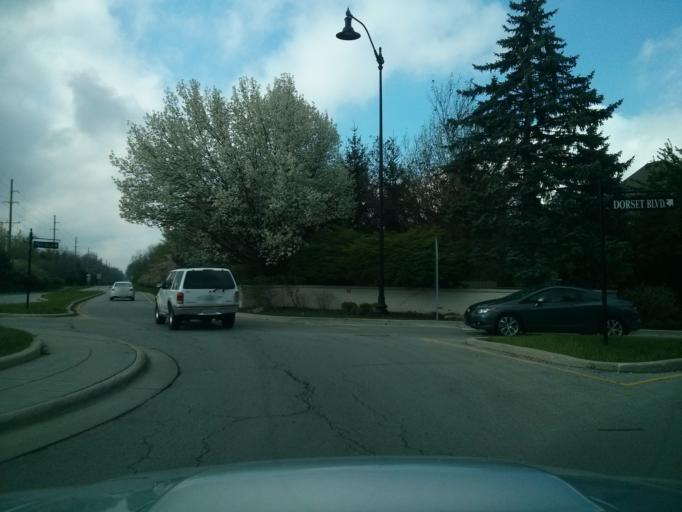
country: US
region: Indiana
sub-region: Hamilton County
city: Carmel
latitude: 39.9740
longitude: -86.1648
